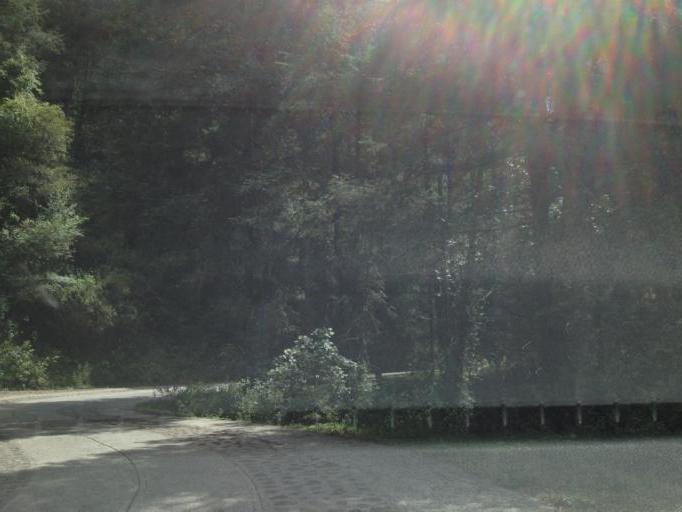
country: MX
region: Hidalgo
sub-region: Pachuca de Soto
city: San Miguel Cerezo (El Cerezo)
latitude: 20.2126
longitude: -98.6878
